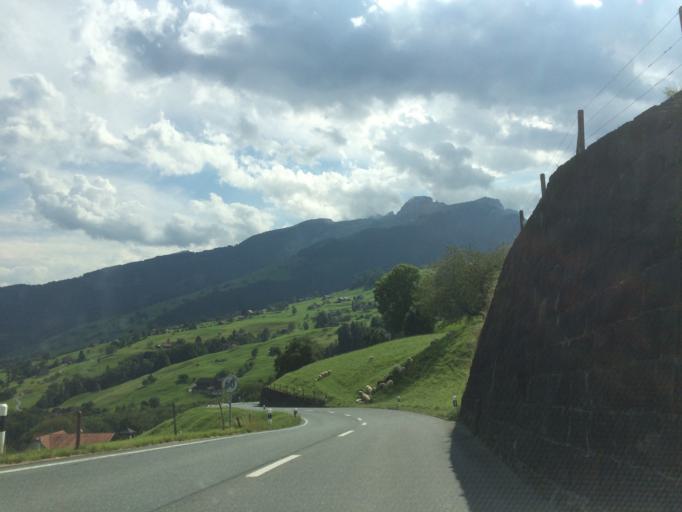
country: CH
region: Saint Gallen
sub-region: Wahlkreis Werdenberg
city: Gams
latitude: 47.1979
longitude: 9.4321
